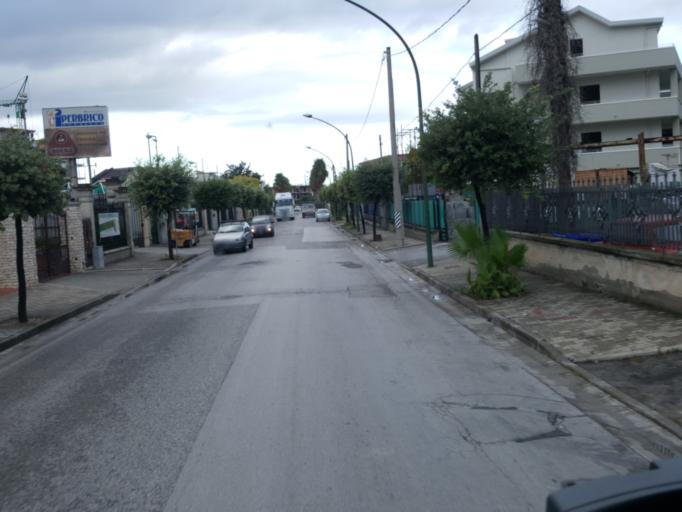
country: IT
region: Campania
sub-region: Provincia di Napoli
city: Palma Campania
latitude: 40.8584
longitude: 14.5512
